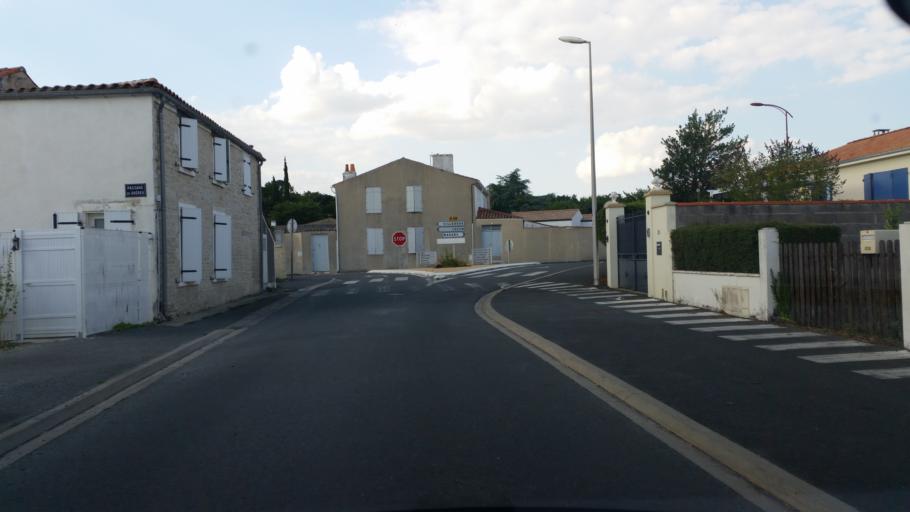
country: FR
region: Poitou-Charentes
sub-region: Departement de la Charente-Maritime
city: Andilly
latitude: 46.2532
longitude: -1.0245
